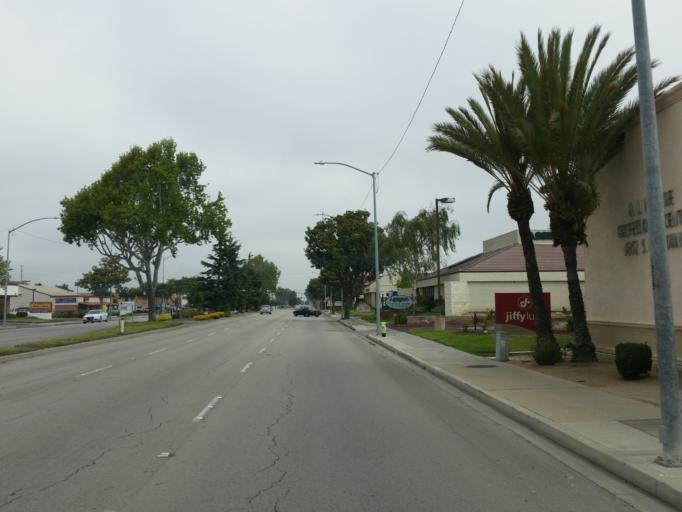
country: US
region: California
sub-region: Santa Barbara County
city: Santa Maria
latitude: 34.9271
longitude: -120.4359
